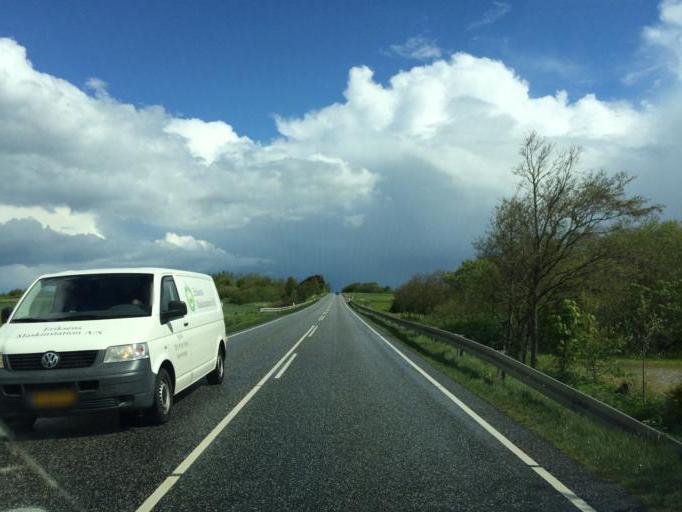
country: DK
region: Central Jutland
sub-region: Holstebro Kommune
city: Vinderup
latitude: 56.4244
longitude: 8.7077
